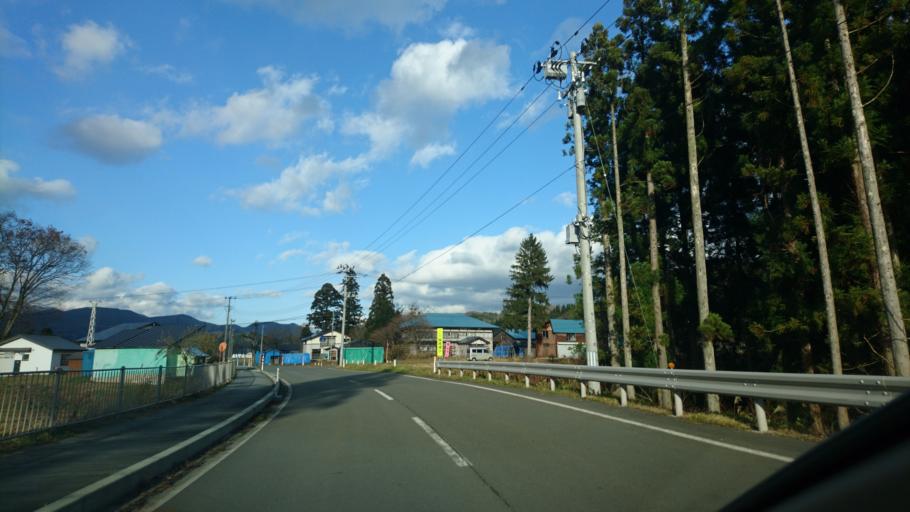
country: JP
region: Akita
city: Kakunodatemachi
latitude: 39.4511
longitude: 140.7837
